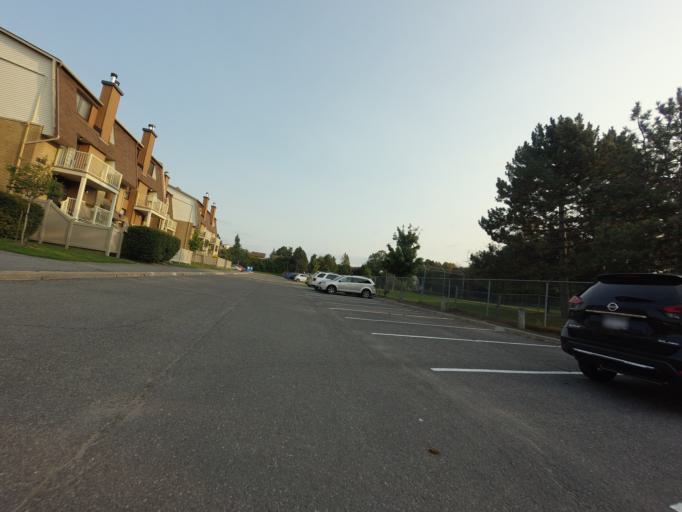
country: CA
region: Ontario
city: Bells Corners
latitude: 45.2794
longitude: -75.7591
